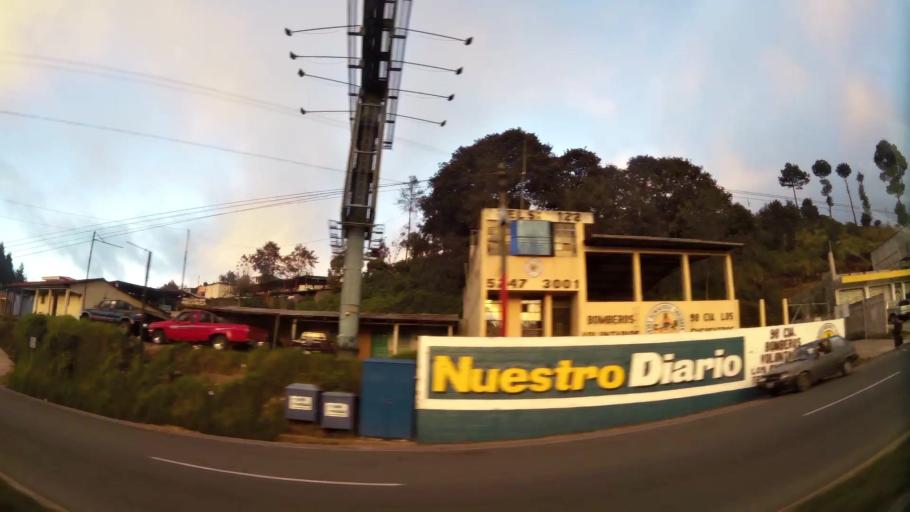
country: GT
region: Solola
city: Concepcion
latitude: 14.8520
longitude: -91.1471
